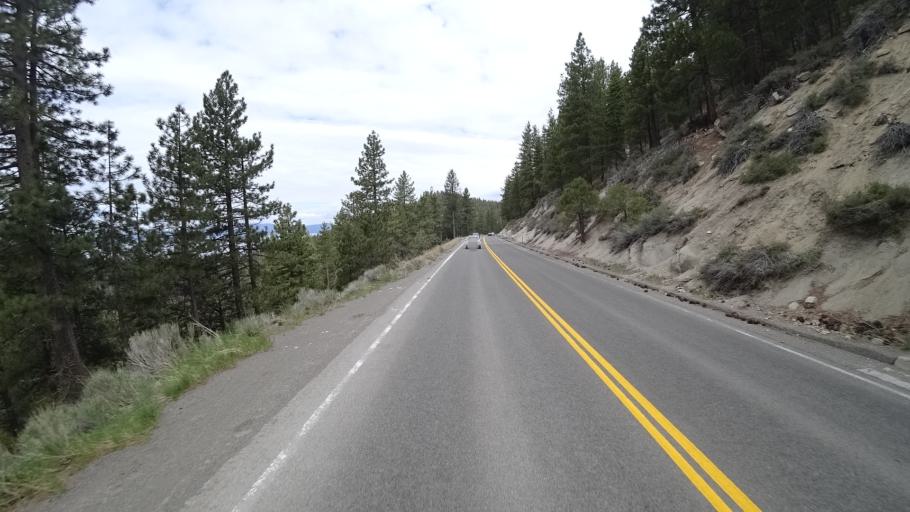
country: US
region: Nevada
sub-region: Washoe County
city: Incline Village
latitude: 39.1227
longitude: -119.9291
